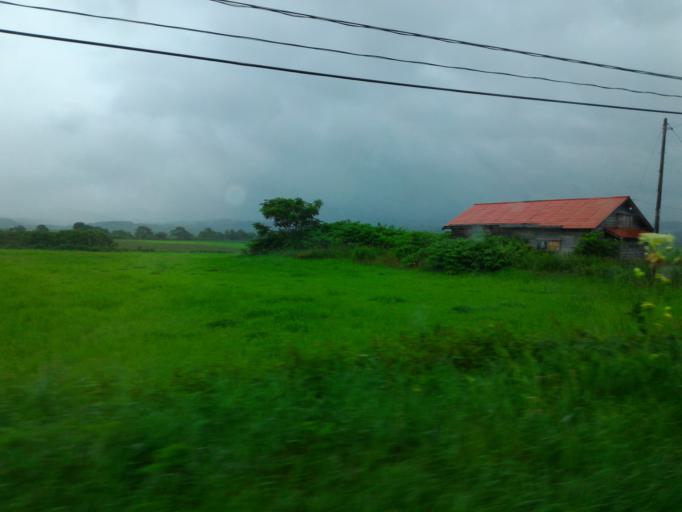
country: JP
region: Hokkaido
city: Makubetsu
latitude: 44.8345
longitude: 142.0574
